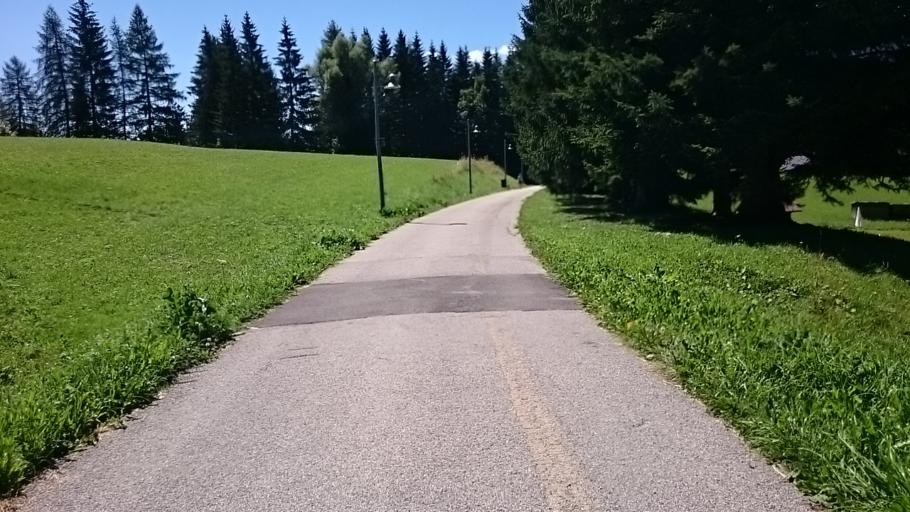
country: IT
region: Veneto
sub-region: Provincia di Belluno
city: Cortina d'Ampezzo
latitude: 46.5520
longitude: 12.1311
